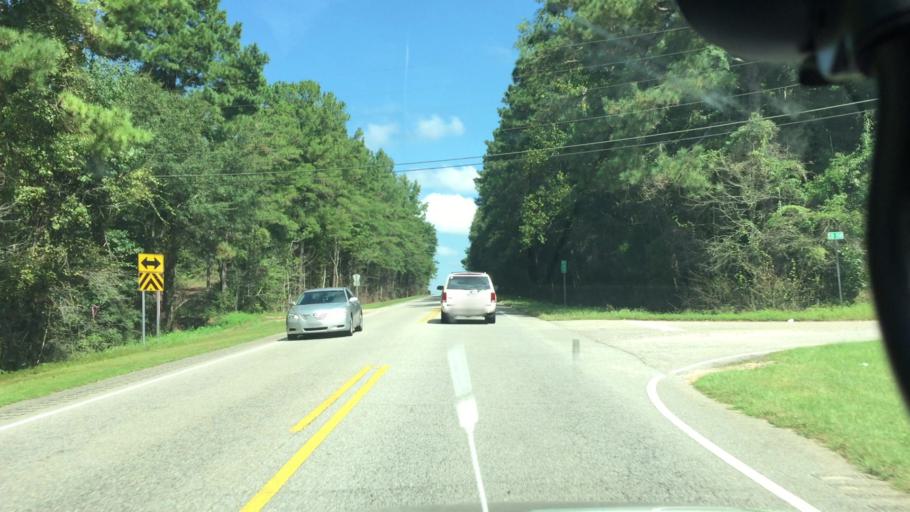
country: US
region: Alabama
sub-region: Coffee County
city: New Brockton
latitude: 31.4071
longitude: -85.8824
